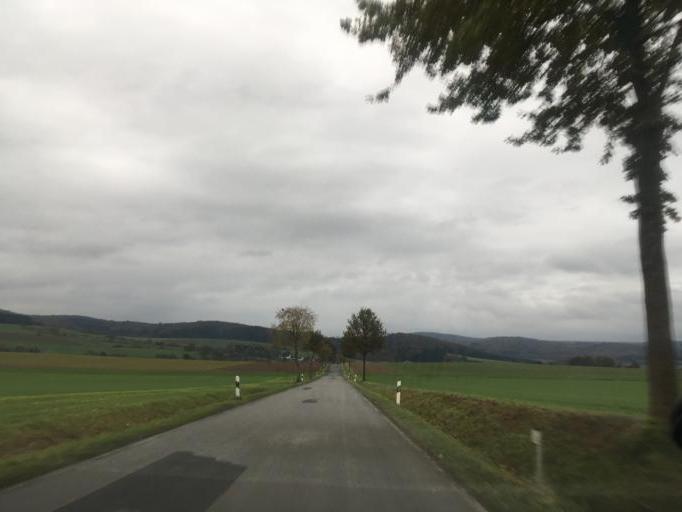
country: DE
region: Lower Saxony
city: Uslar
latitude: 51.6687
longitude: 9.6629
